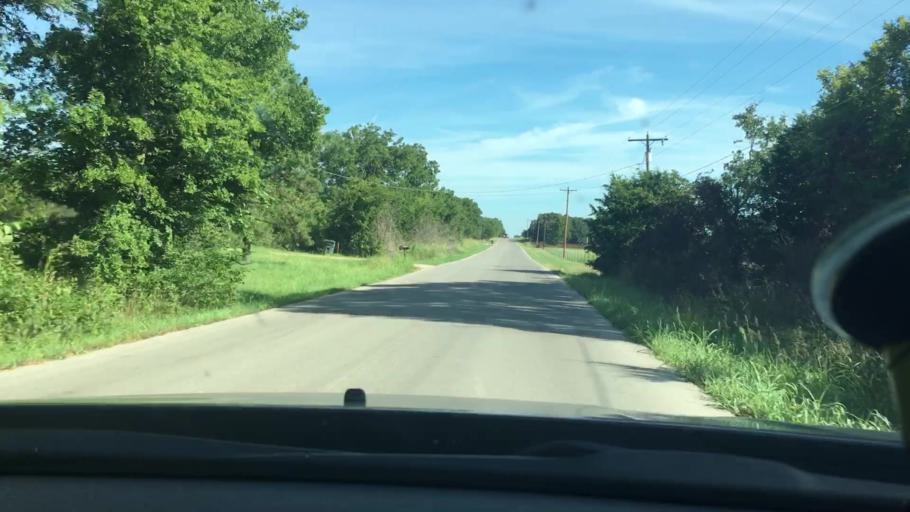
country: US
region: Oklahoma
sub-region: Carter County
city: Lone Grove
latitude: 34.2323
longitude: -97.2474
